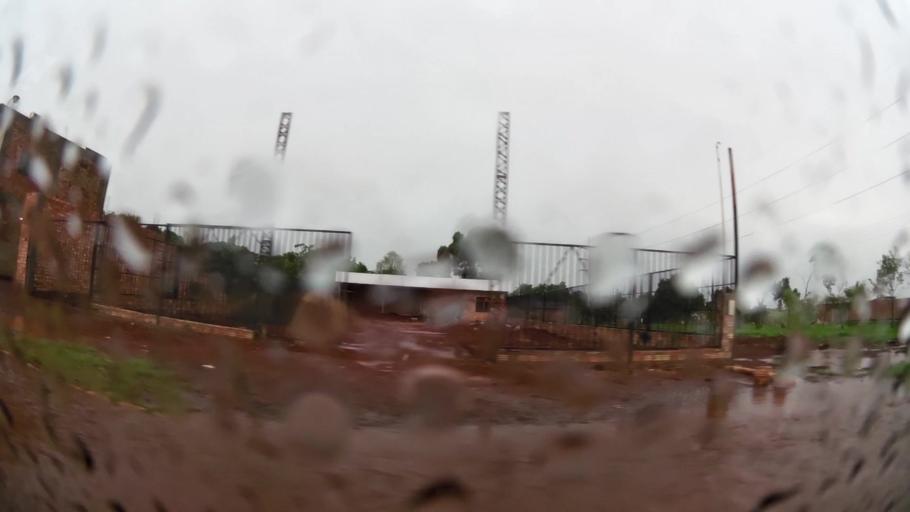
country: PY
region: Alto Parana
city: Presidente Franco
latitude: -25.5228
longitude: -54.6764
